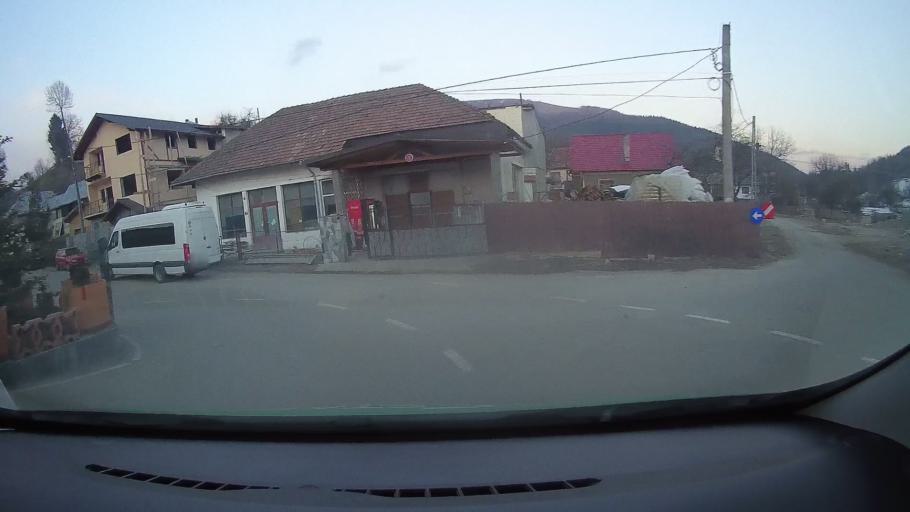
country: RO
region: Prahova
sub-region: Comuna Secaria
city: Secaria
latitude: 45.2727
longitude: 25.6860
